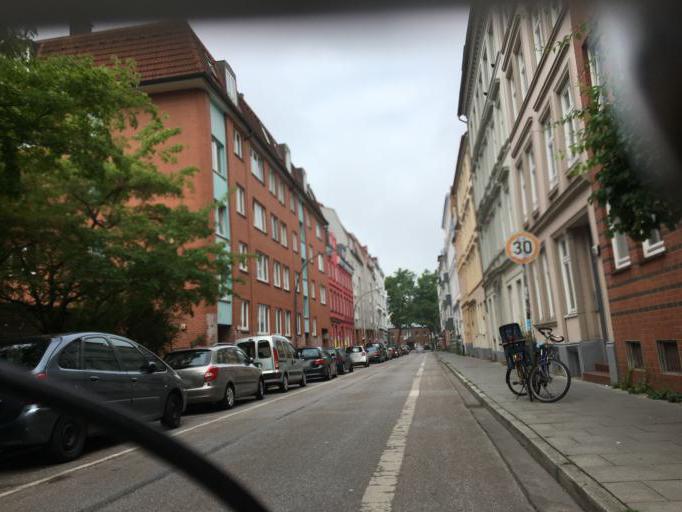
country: DE
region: Hamburg
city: Altona
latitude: 53.5503
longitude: 9.9321
